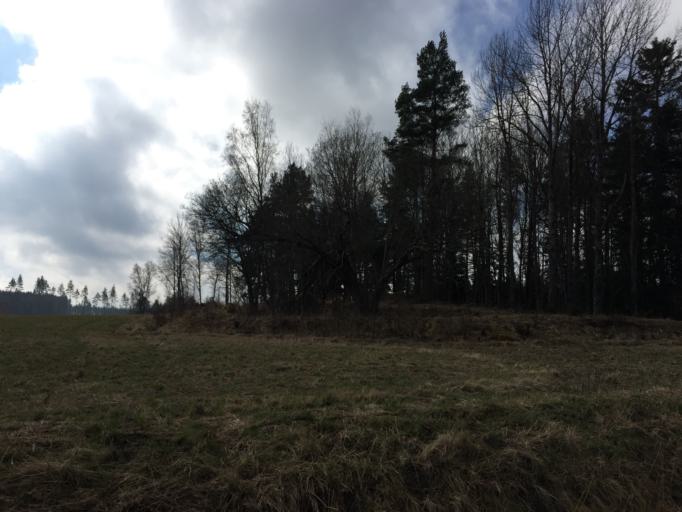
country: SE
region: Soedermanland
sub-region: Gnesta Kommun
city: Gnesta
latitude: 59.0266
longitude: 17.1983
